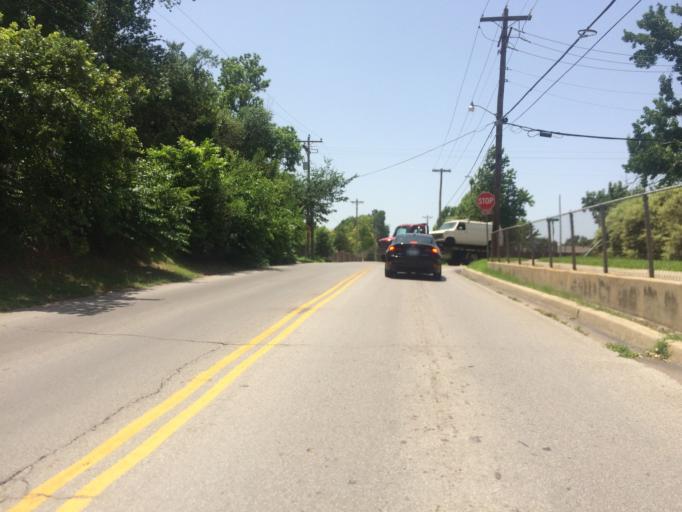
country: US
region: Oklahoma
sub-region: Cleveland County
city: Norman
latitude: 35.1894
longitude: -97.4587
